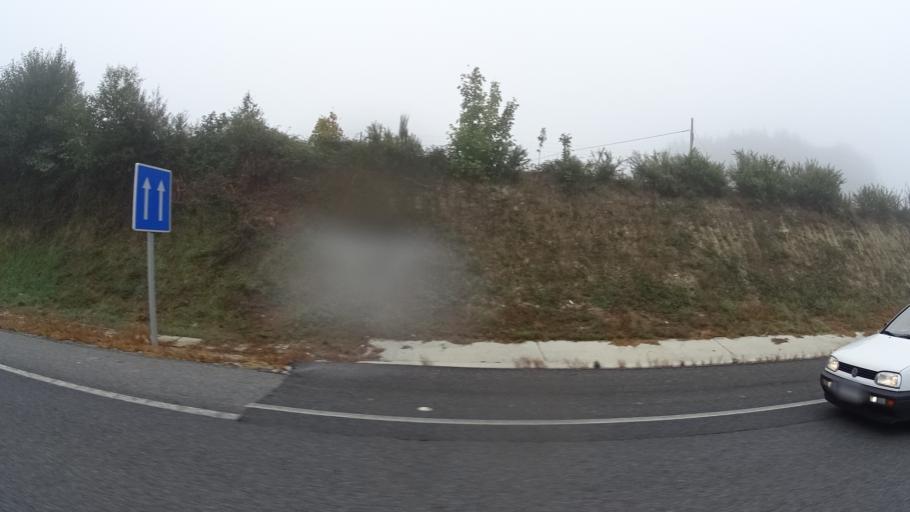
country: ES
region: Galicia
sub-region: Provincia de Lugo
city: Lugo
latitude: 42.9804
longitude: -7.5015
